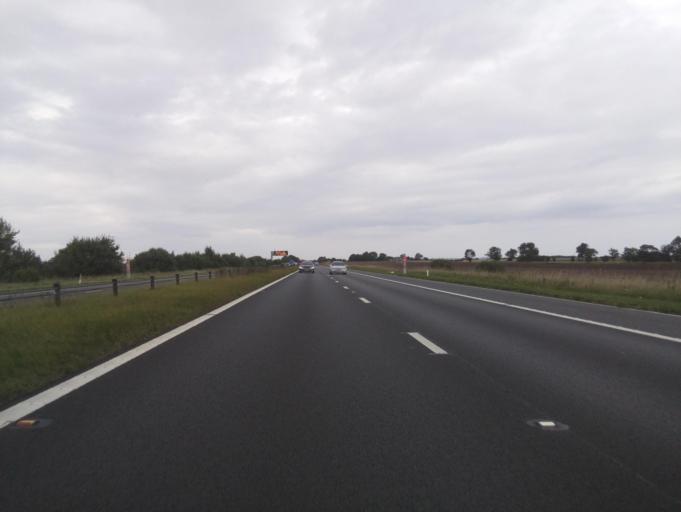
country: GB
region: England
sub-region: County Durham
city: Newton Aycliffe
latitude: 54.6293
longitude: -1.5249
